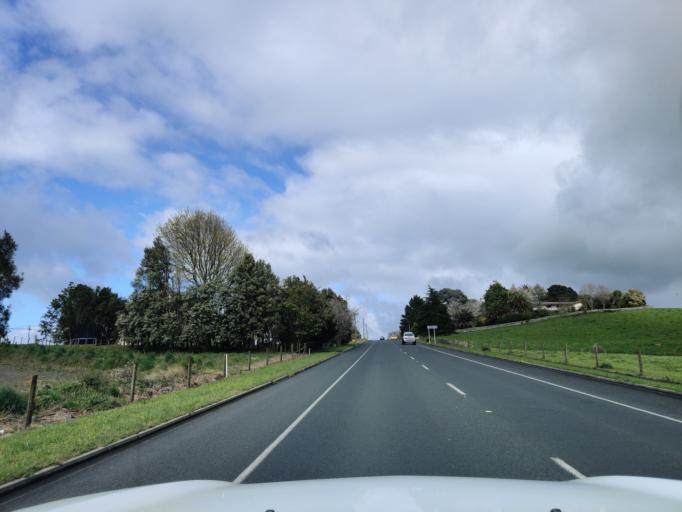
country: NZ
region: Waikato
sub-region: Hamilton City
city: Hamilton
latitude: -37.8284
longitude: 175.2218
